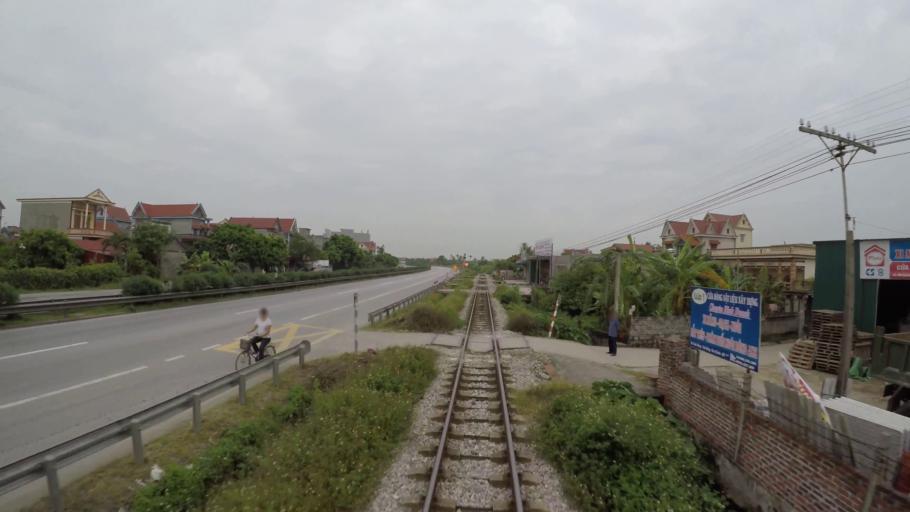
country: VN
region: Hai Duong
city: Phu Thai
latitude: 20.9758
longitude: 106.4334
